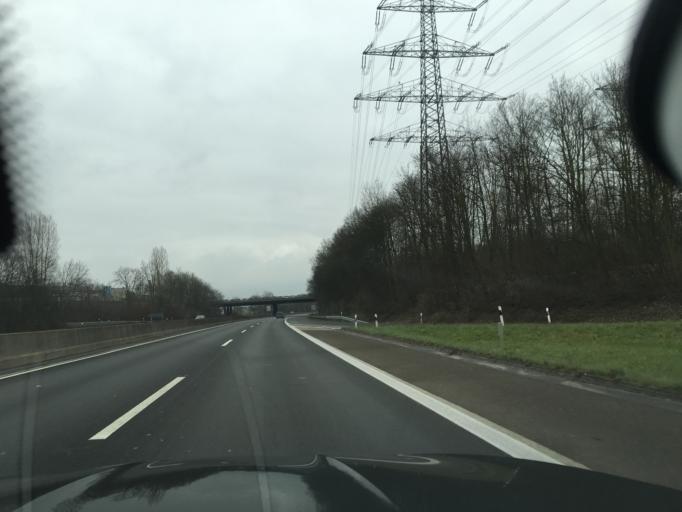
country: DE
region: North Rhine-Westphalia
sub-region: Regierungsbezirk Koln
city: Troisdorf
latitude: 50.8091
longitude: 7.1318
